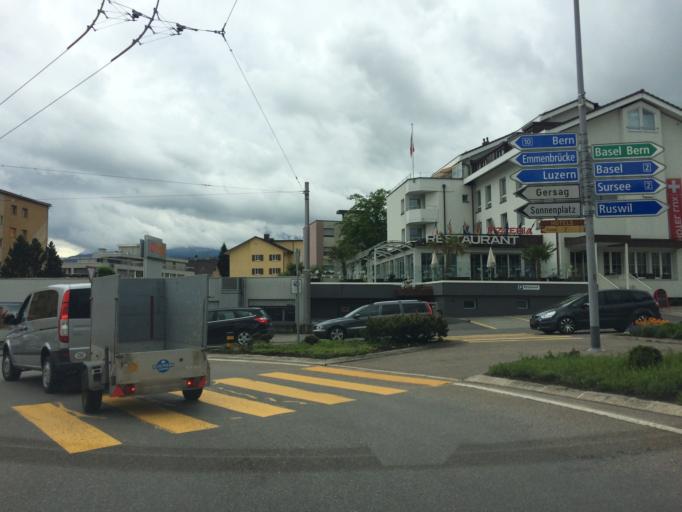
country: CH
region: Lucerne
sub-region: Hochdorf District
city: Emmen
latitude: 47.0815
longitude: 8.2712
